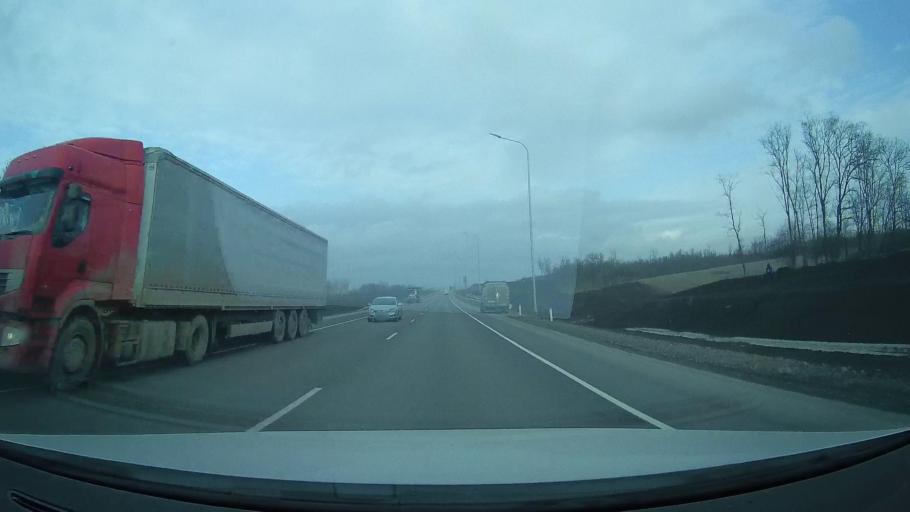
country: RU
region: Rostov
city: Grushevskaya
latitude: 47.4181
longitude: 39.8617
